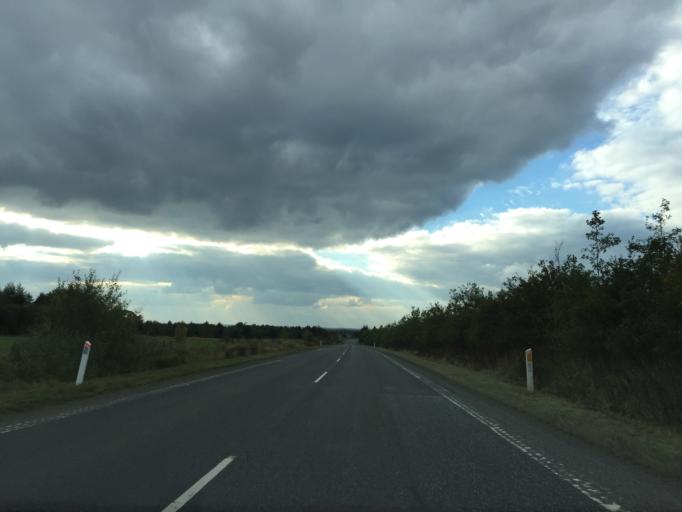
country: DK
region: Central Jutland
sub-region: Favrskov Kommune
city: Ulstrup
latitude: 56.3239
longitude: 9.8091
